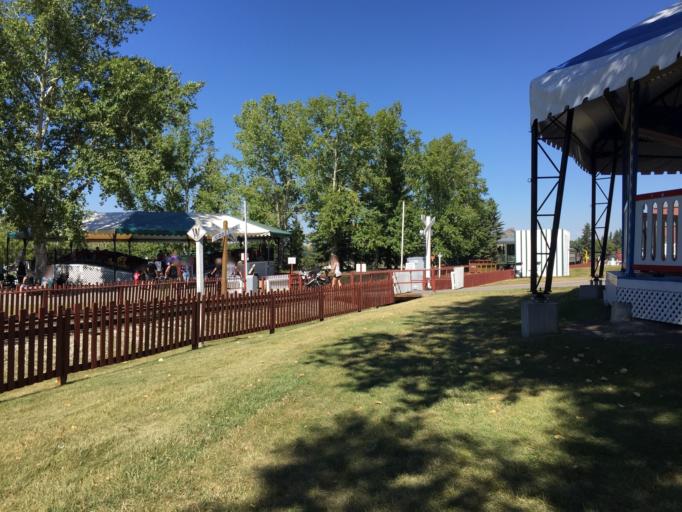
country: CA
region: Alberta
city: Calgary
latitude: 50.9838
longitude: -114.1090
